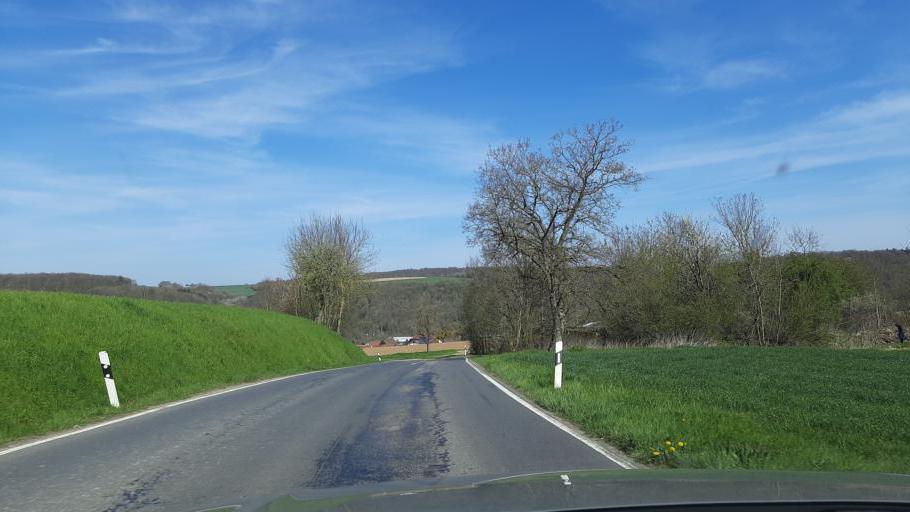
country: DE
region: Baden-Wuerttemberg
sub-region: Regierungsbezirk Stuttgart
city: Jagsthausen
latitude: 49.3227
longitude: 9.4947
